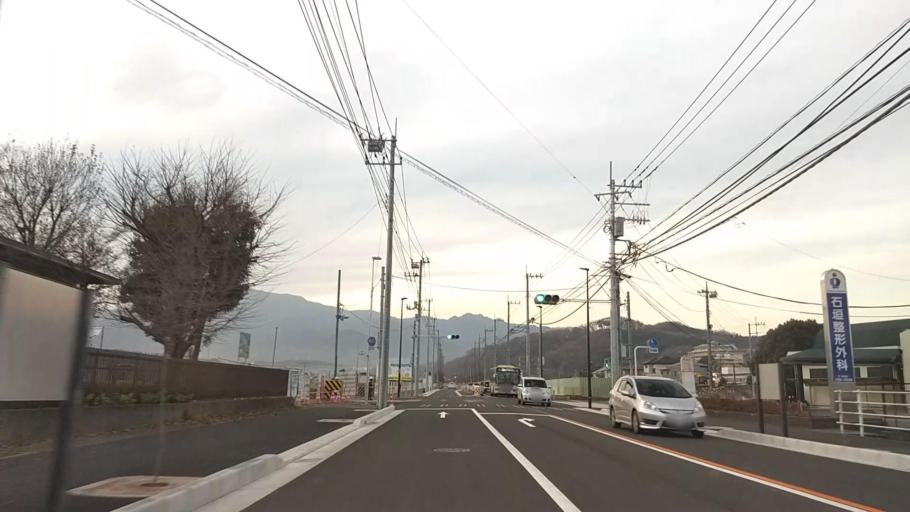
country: JP
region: Kanagawa
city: Atsugi
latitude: 35.4315
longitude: 139.3282
